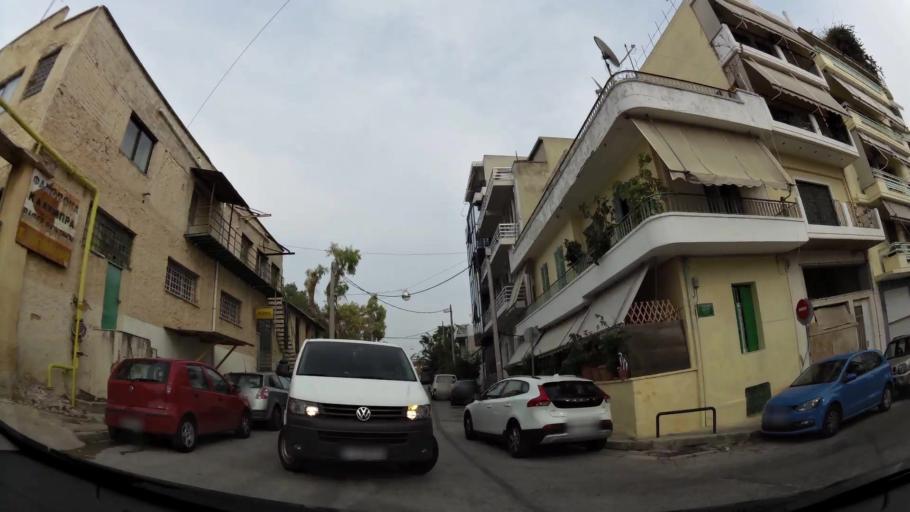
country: GR
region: Attica
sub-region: Nomarchia Athinas
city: Nea Ionia
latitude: 38.0406
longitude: 23.7584
